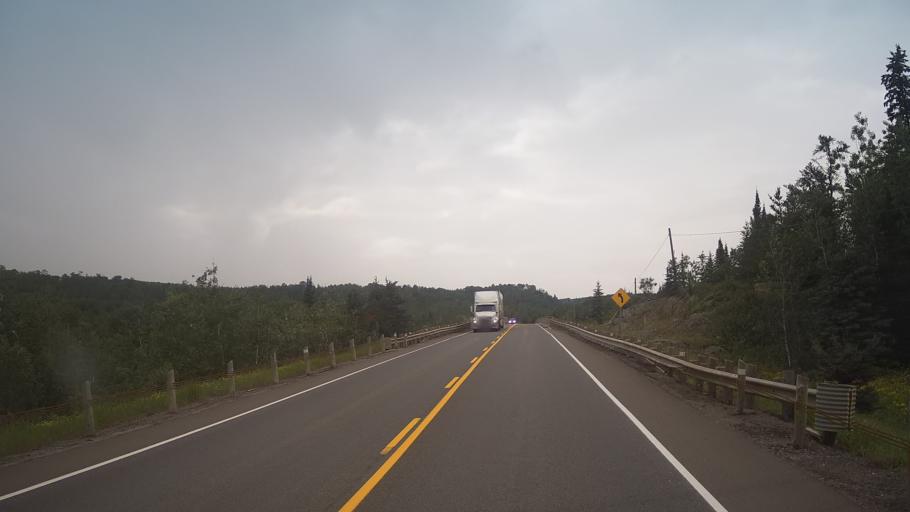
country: CA
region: Ontario
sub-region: Thunder Bay District
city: Thunder Bay
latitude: 48.5353
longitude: -89.5930
